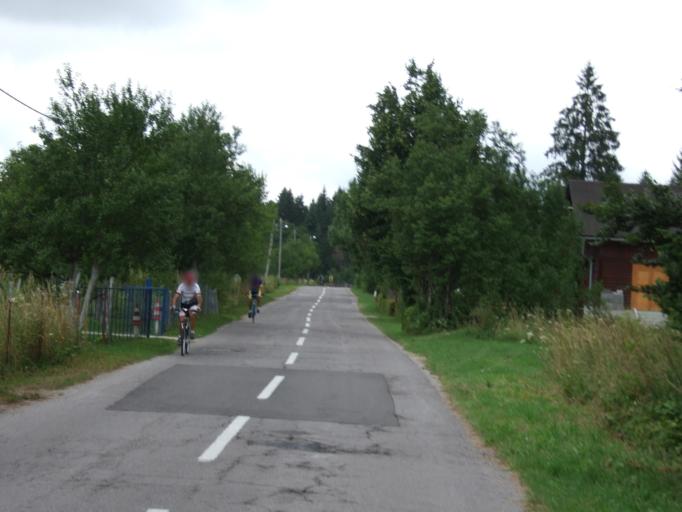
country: HR
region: Licko-Senjska
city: Jezerce
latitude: 44.9493
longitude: 15.5345
